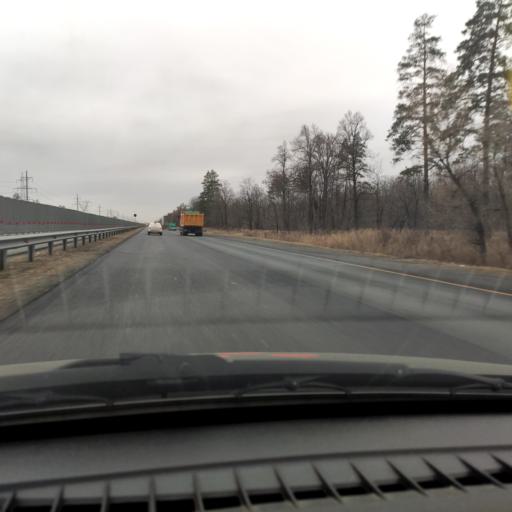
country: RU
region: Samara
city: Pribrezhnyy
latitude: 53.5156
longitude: 49.8630
